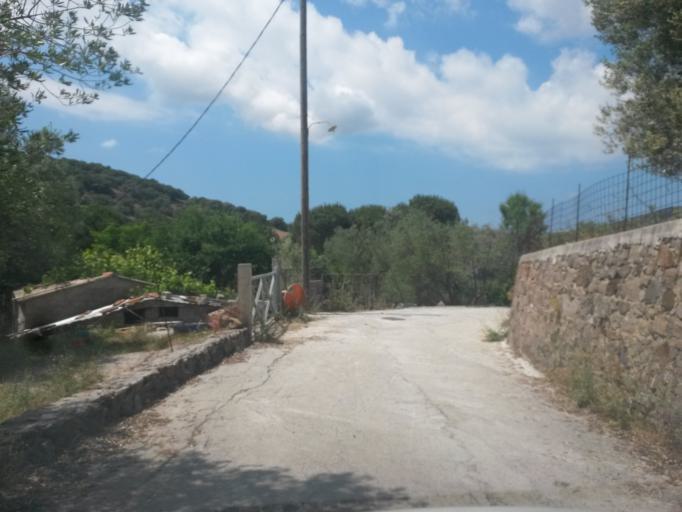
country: GR
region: North Aegean
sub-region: Nomos Lesvou
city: Eresos
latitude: 39.2281
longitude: 26.0511
